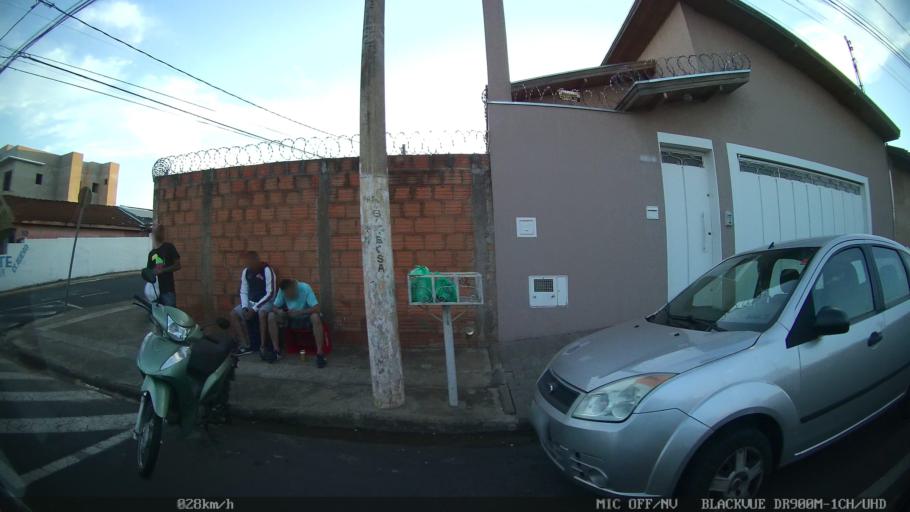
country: BR
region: Sao Paulo
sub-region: Franca
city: Franca
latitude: -20.5208
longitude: -47.4066
